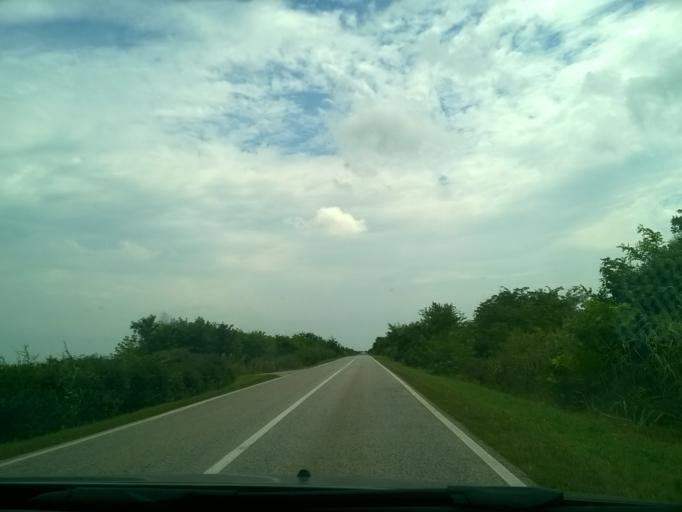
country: RS
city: Lazarevo
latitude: 45.3888
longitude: 20.5953
